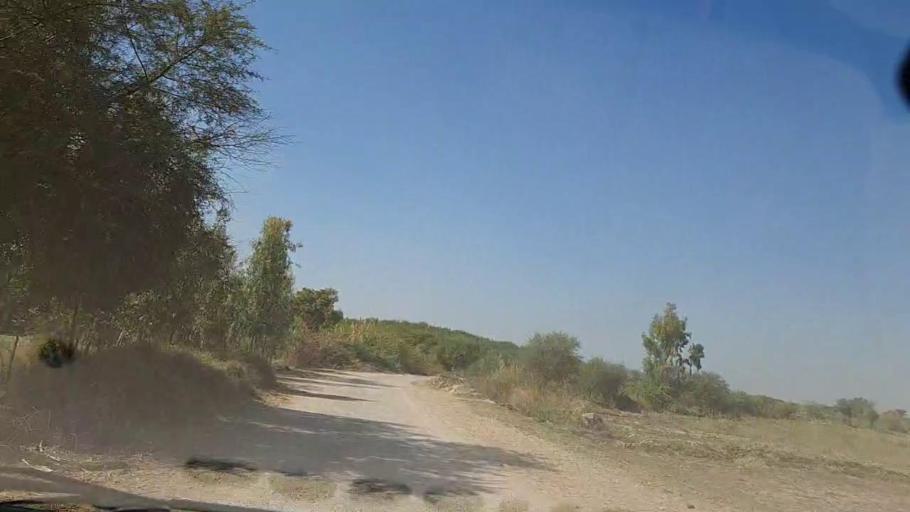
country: PK
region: Sindh
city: Mirwah Gorchani
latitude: 25.3827
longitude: 68.9727
